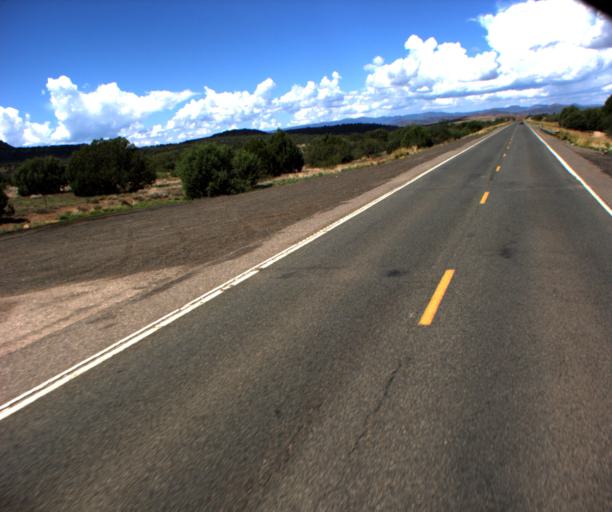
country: US
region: Arizona
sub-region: Yavapai County
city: Camp Verde
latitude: 34.5148
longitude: -111.9990
